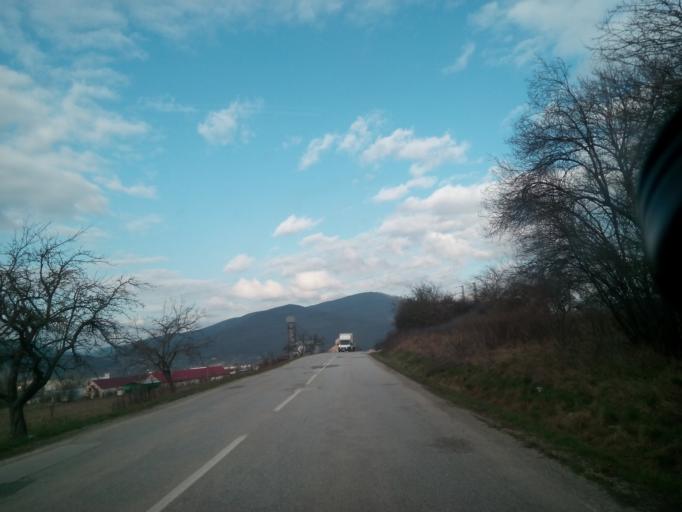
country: SK
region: Kosicky
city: Roznava
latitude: 48.6529
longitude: 20.5554
